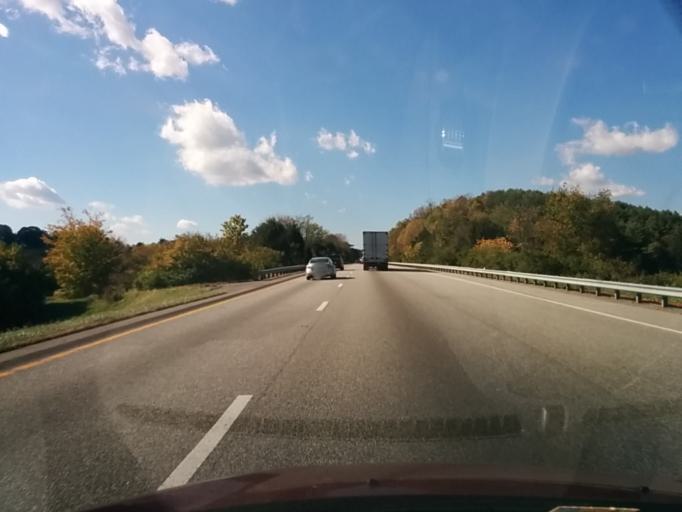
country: US
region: Virginia
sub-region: Botetourt County
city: Fincastle
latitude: 37.4541
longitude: -79.8463
